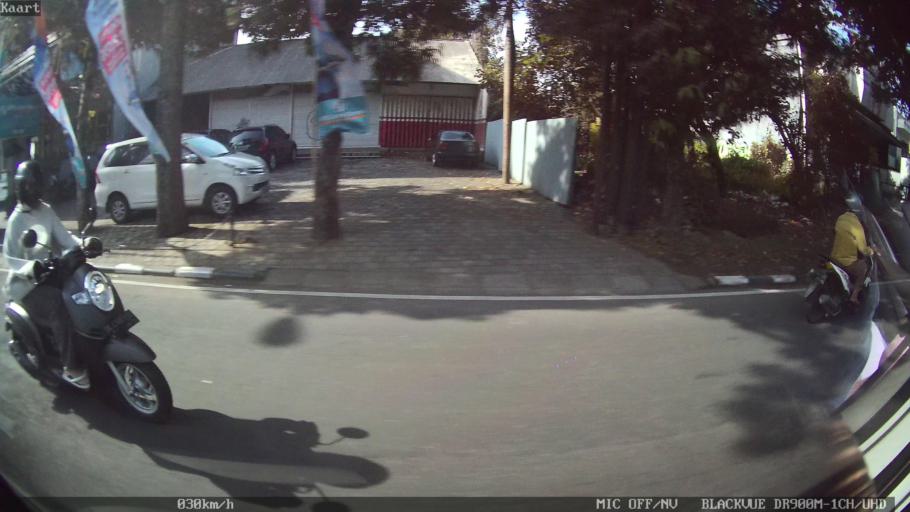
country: ID
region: Bali
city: Tabanan
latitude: -8.5513
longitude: 115.1279
